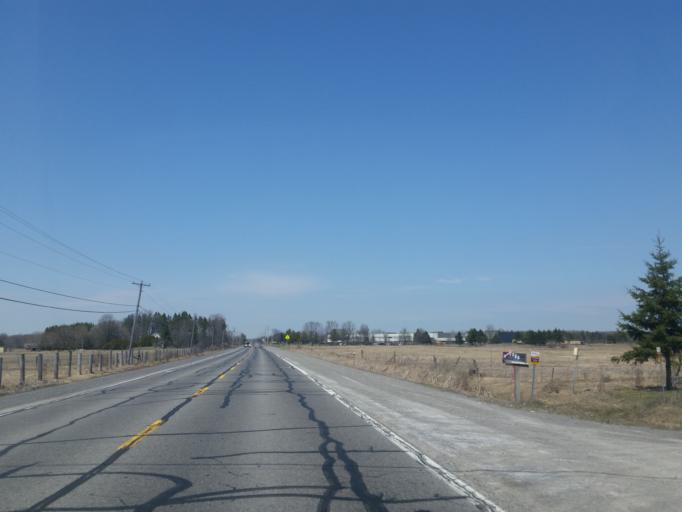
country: CA
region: Ontario
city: Bells Corners
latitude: 45.4297
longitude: -76.0305
